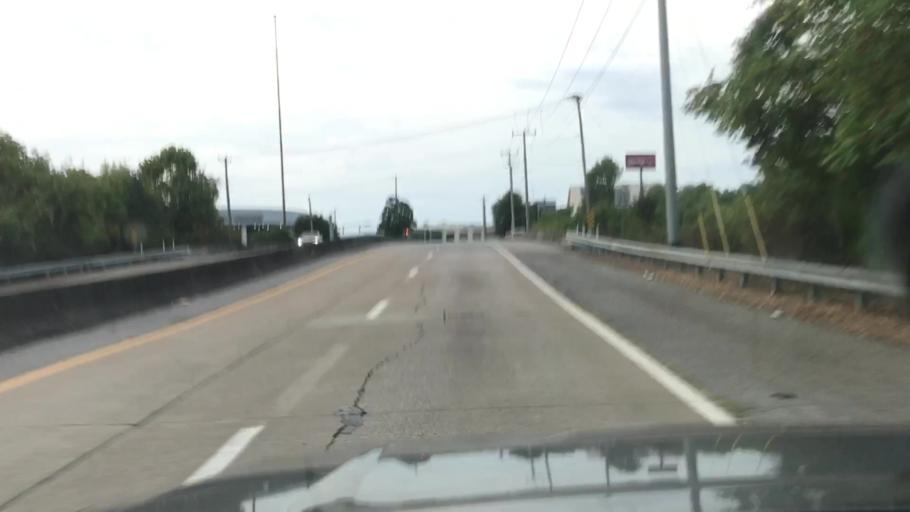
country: US
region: Tennessee
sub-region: Rutherford County
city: La Vergne
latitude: 36.0430
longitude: -86.6498
